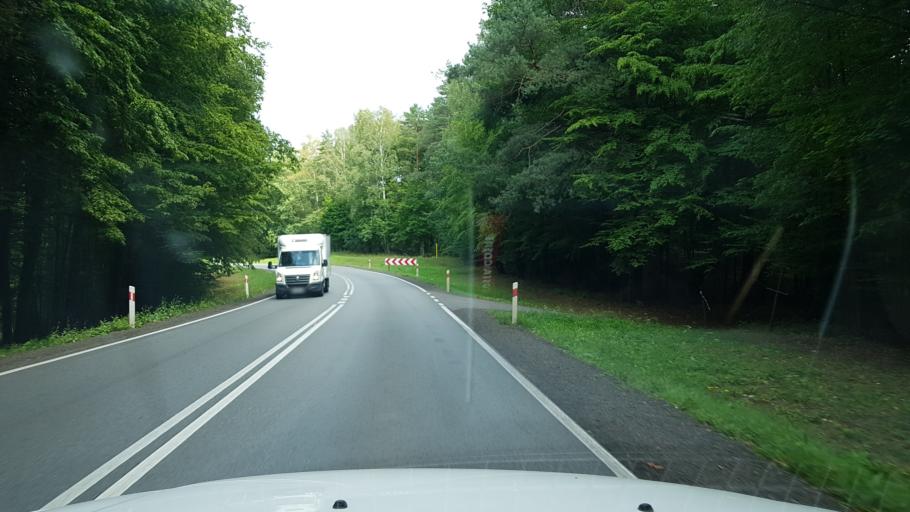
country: PL
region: West Pomeranian Voivodeship
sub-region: Powiat walecki
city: Walcz
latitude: 53.2934
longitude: 16.5247
